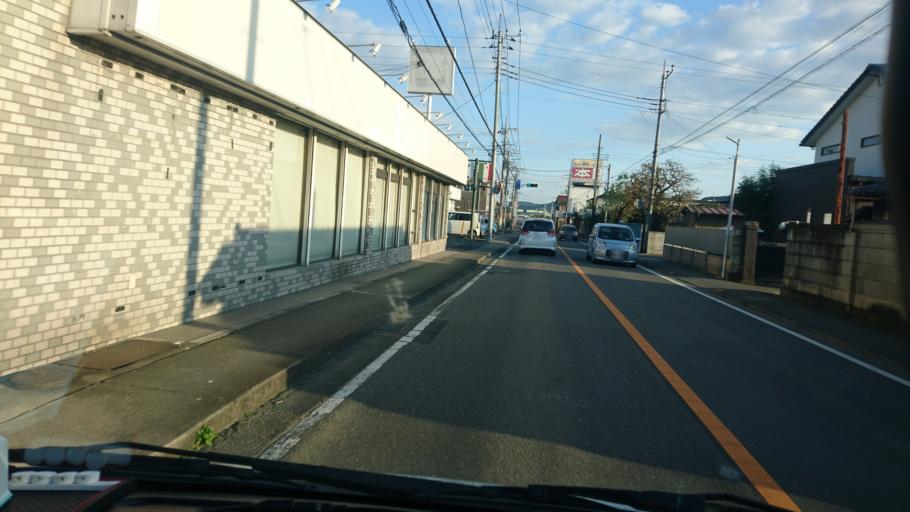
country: JP
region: Gunma
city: Kiryu
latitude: 36.4002
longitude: 139.3208
